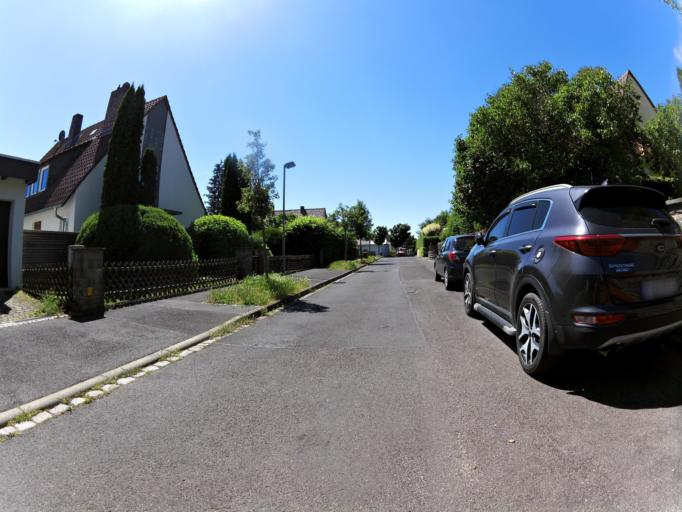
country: DE
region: Bavaria
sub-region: Regierungsbezirk Unterfranken
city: Ochsenfurt
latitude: 49.6726
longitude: 10.0625
